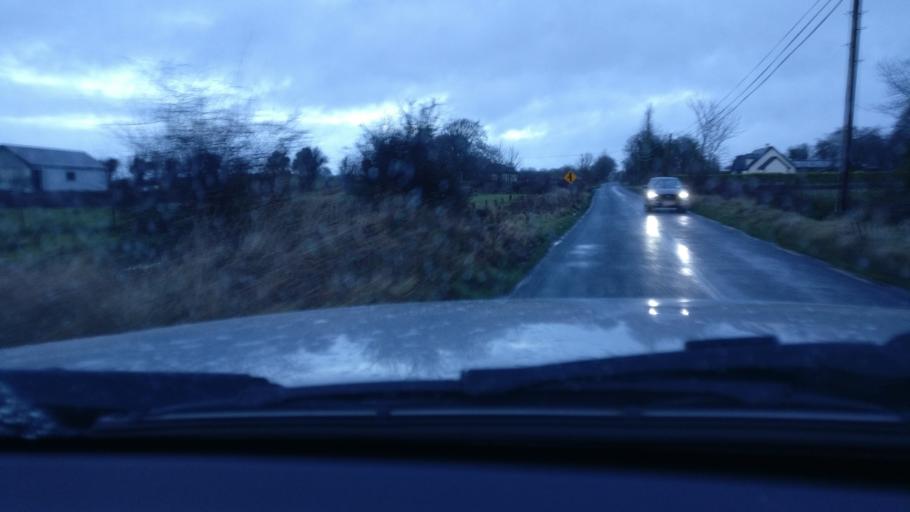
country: IE
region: Connaught
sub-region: County Galway
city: Ballinasloe
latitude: 53.2458
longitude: -8.2665
